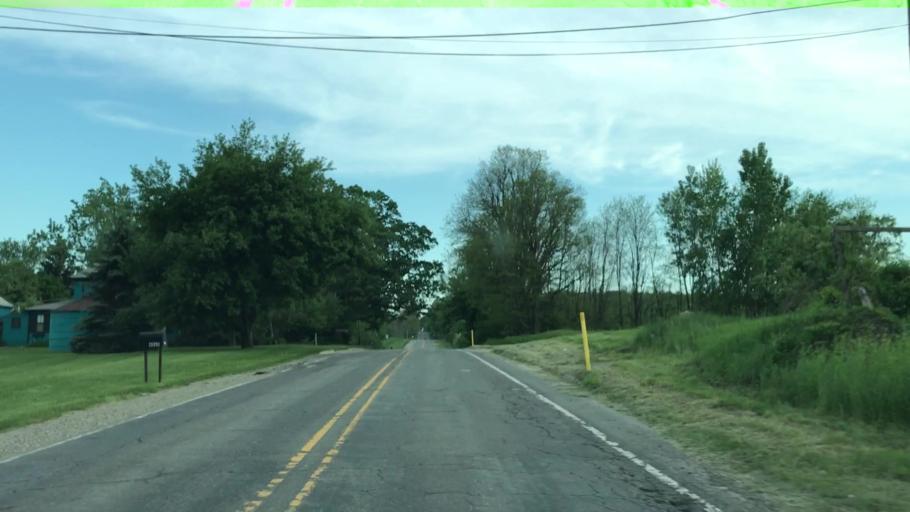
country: US
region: Michigan
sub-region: Lapeer County
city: Almont
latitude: 42.9208
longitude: -83.1436
